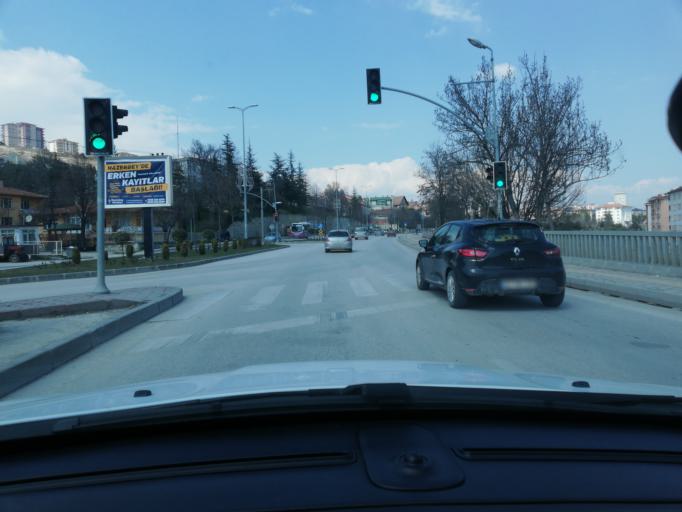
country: TR
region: Kastamonu
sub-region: Cide
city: Kastamonu
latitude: 41.3976
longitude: 33.7812
